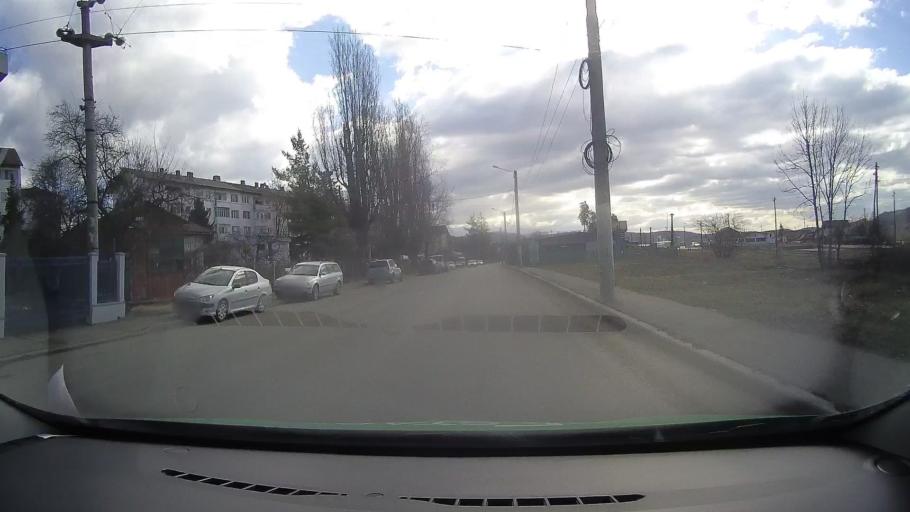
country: RO
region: Dambovita
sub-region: Oras Pucioasa
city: Pucioasa
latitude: 45.0769
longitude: 25.4304
